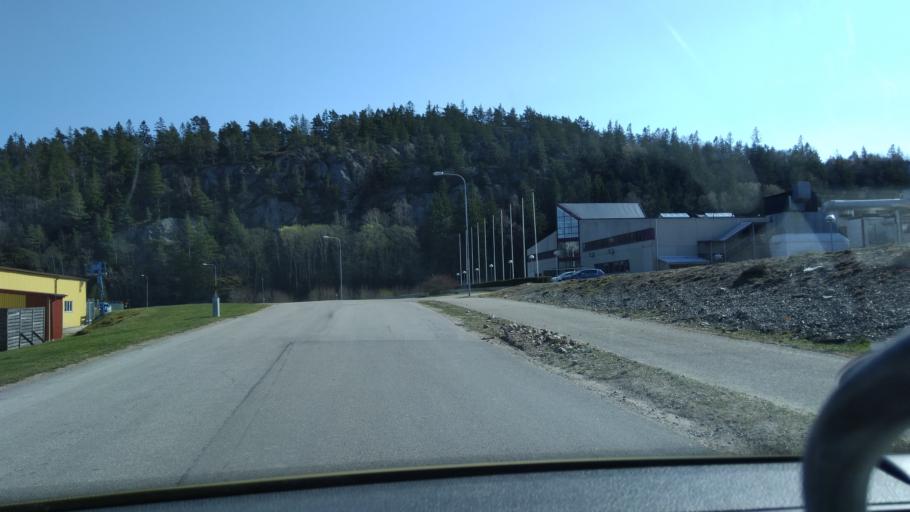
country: SE
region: Vaestra Goetaland
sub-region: Orust
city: Henan
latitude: 58.2305
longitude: 11.6527
